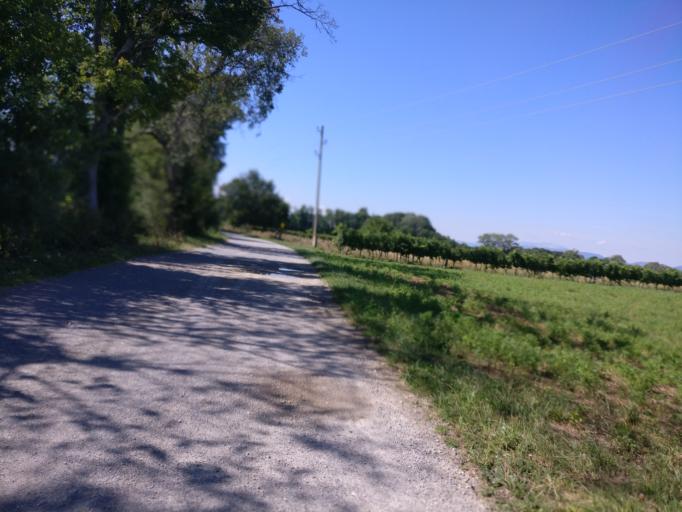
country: AT
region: Lower Austria
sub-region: Politischer Bezirk Baden
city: Pottendorf
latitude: 47.9087
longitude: 16.3535
